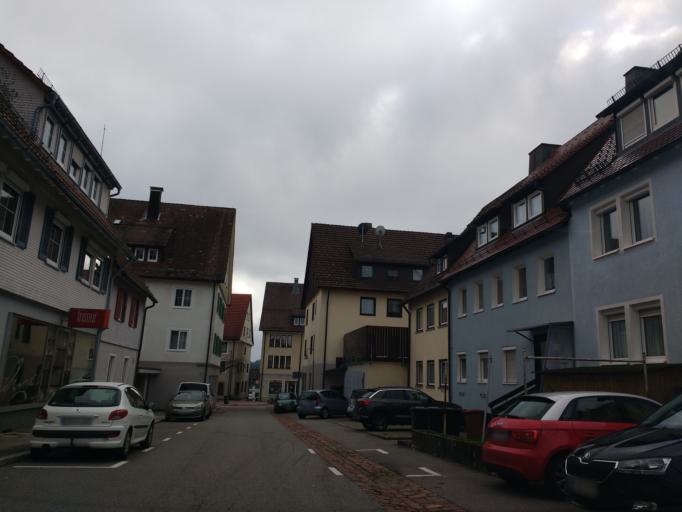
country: DE
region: Baden-Wuerttemberg
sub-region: Karlsruhe Region
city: Freudenstadt
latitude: 48.4651
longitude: 8.4136
